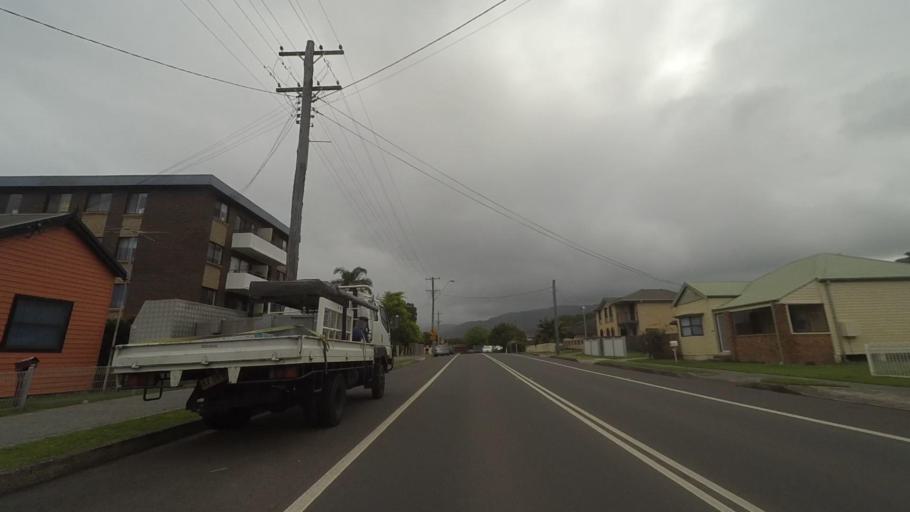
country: AU
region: New South Wales
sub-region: Wollongong
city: Bulli
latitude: -34.3129
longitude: 150.9280
